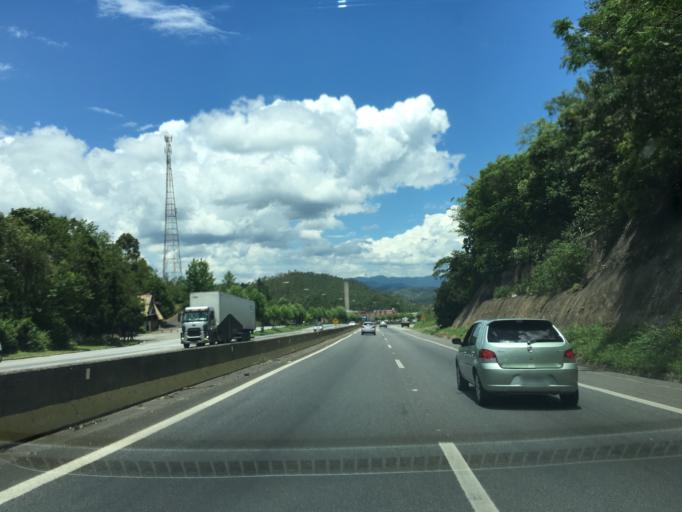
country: BR
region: Sao Paulo
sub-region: Mairipora
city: Mairipora
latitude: -23.2922
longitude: -46.5780
